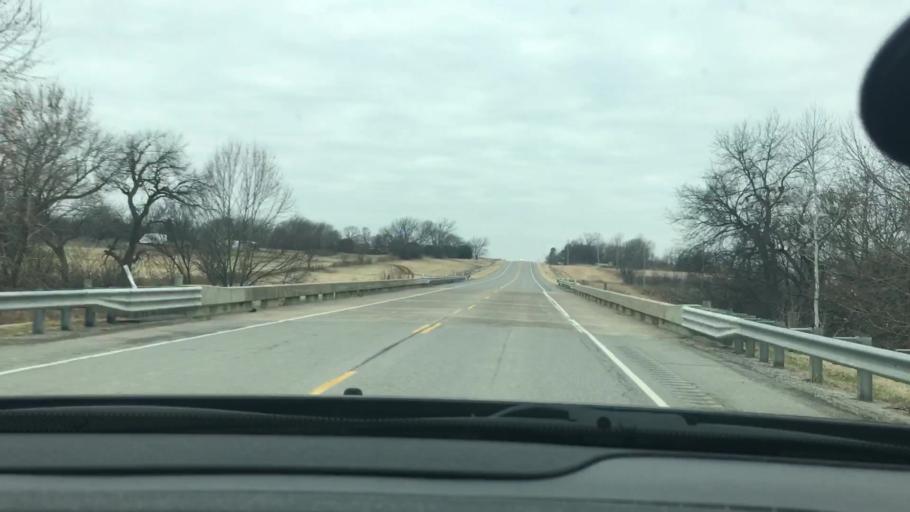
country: US
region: Oklahoma
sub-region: Murray County
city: Davis
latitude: 34.4925
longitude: -97.3806
